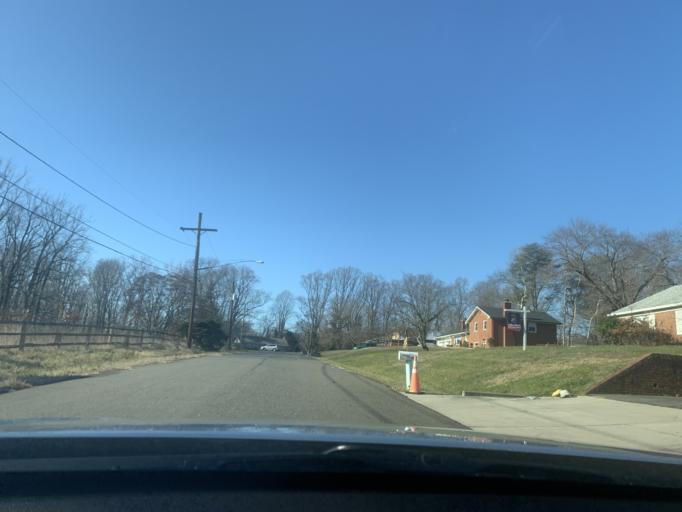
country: US
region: Maryland
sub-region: Prince George's County
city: Camp Springs
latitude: 38.8167
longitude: -76.9210
